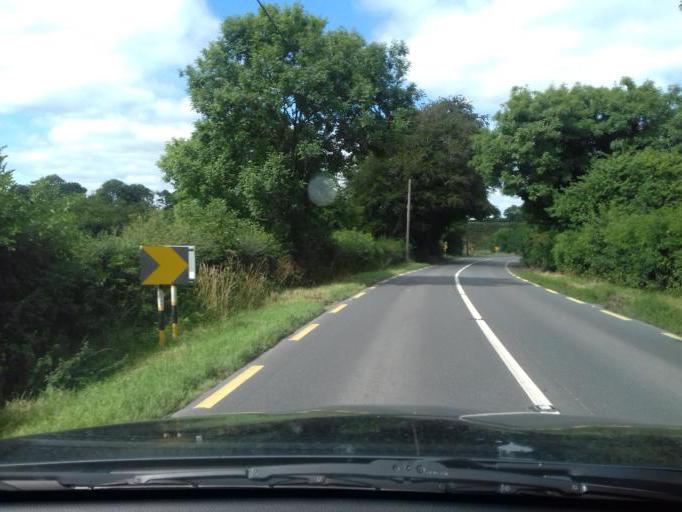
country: IE
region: Leinster
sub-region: Wicklow
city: Baltinglass
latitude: 53.0206
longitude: -6.6456
